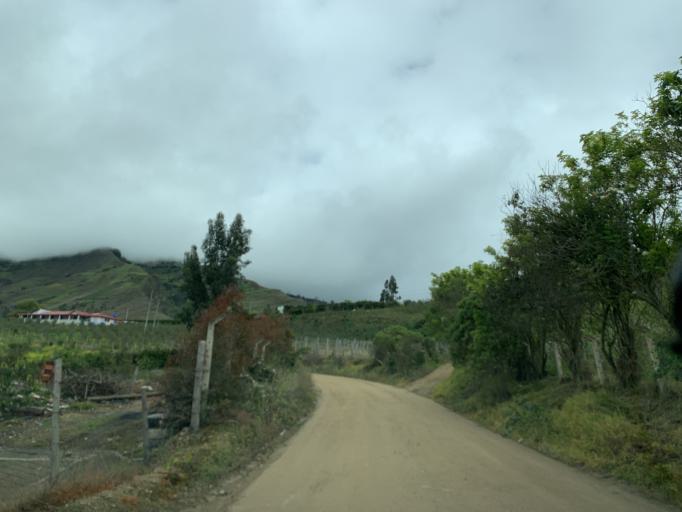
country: CO
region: Boyaca
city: Tibana
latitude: 5.3116
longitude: -73.4266
